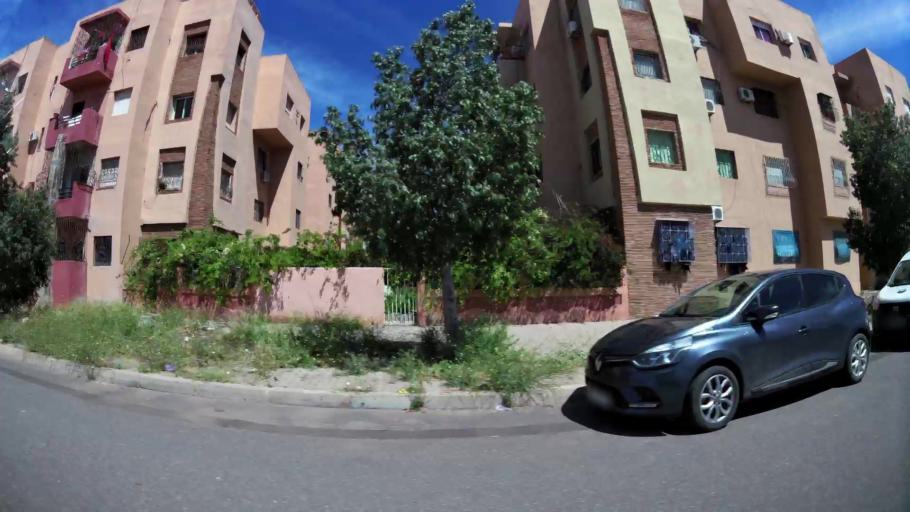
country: MA
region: Marrakech-Tensift-Al Haouz
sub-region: Marrakech
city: Marrakesh
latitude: 31.6418
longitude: -8.0812
